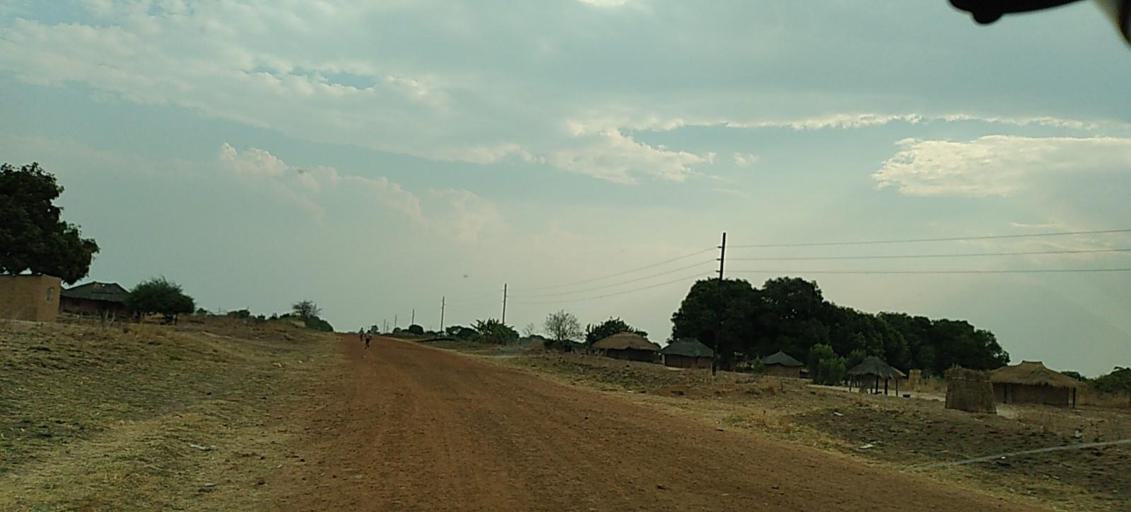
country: ZM
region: North-Western
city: Kabompo
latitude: -13.8680
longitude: 23.6692
